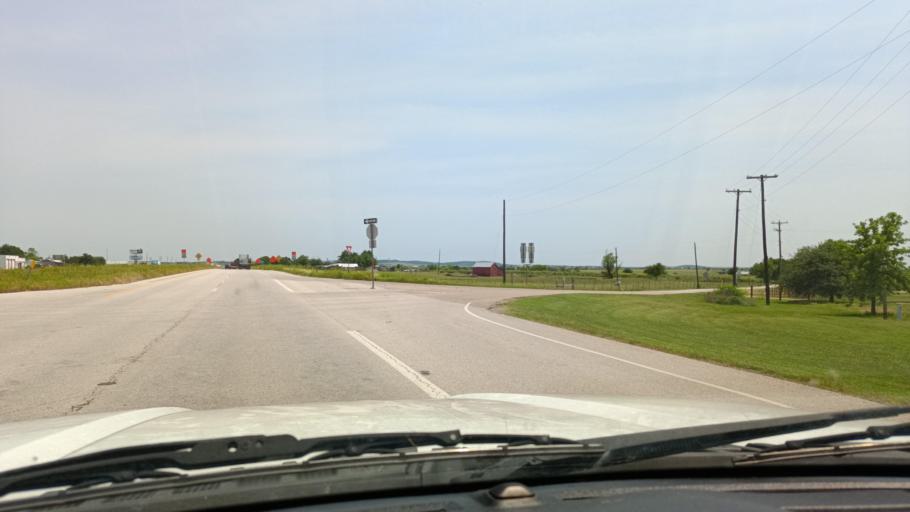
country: US
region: Texas
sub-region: Bell County
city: Little River-Academy
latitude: 31.0005
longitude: -97.2900
